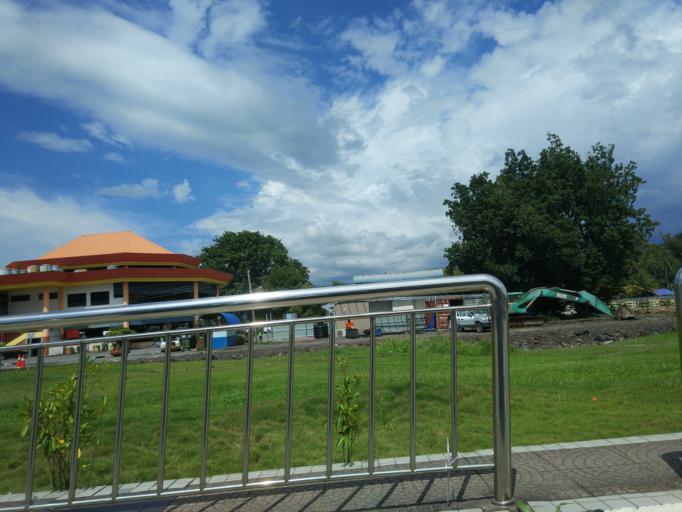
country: BN
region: Temburong
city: Bangar
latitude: 4.8586
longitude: 115.4078
